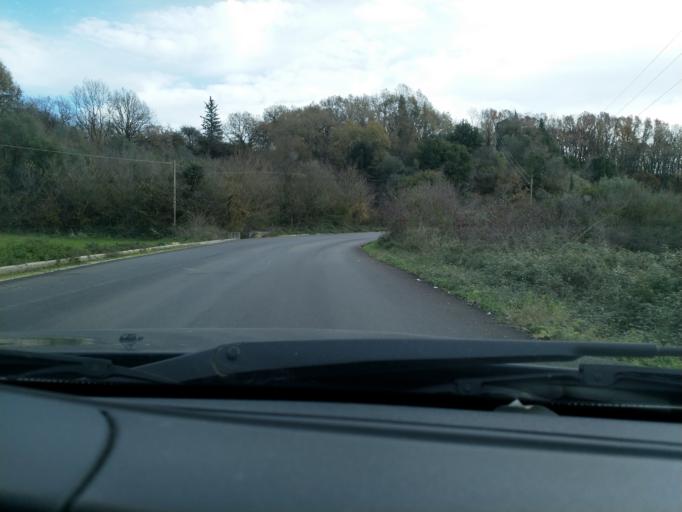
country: GR
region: Epirus
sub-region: Nomos Prevezis
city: Filippiada
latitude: 39.2175
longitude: 20.8589
